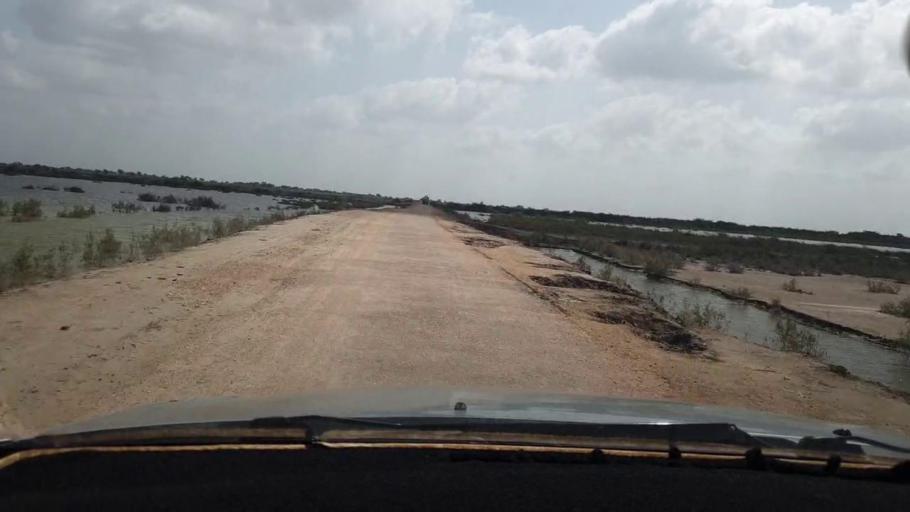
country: PK
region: Sindh
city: Tando Bago
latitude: 24.7207
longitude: 69.1552
